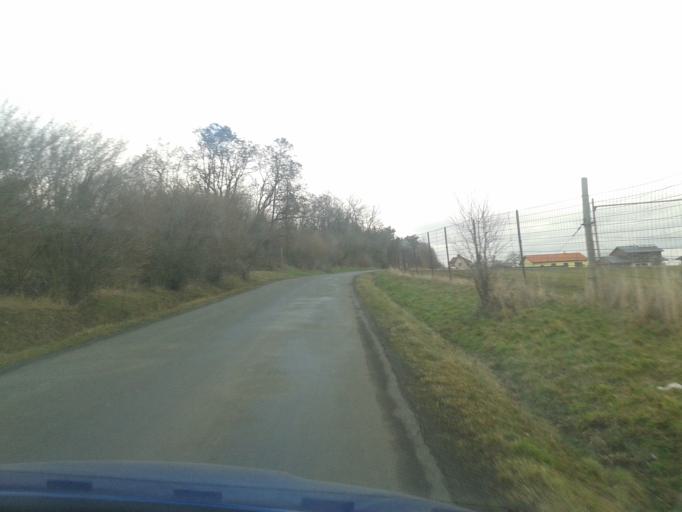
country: CZ
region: Central Bohemia
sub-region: Okres Beroun
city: Beroun
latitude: 49.8966
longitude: 14.1409
